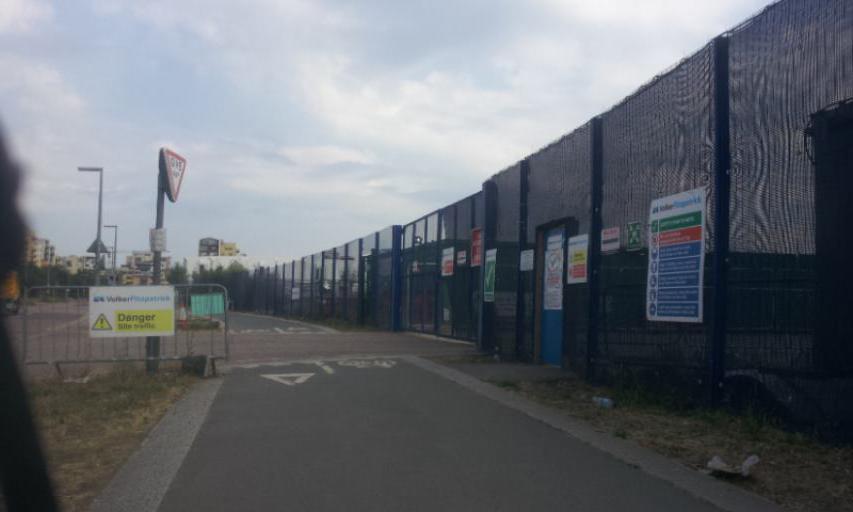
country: GB
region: England
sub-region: Greater London
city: Poplar
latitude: 51.4964
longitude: 0.0084
